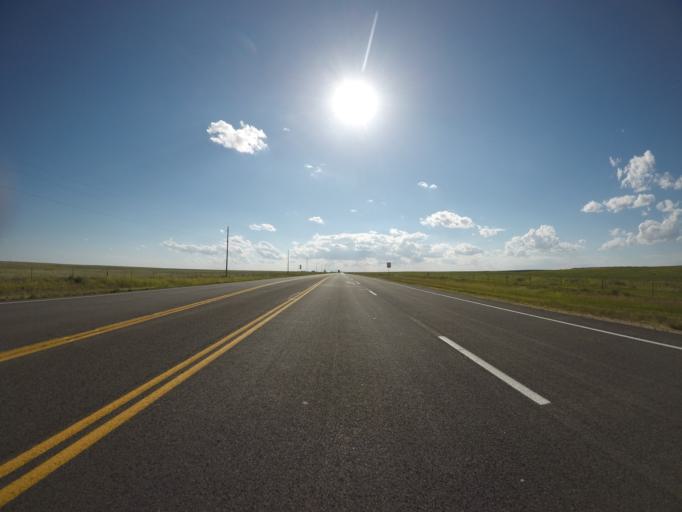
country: US
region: Colorado
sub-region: Morgan County
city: Fort Morgan
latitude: 40.6114
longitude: -103.8042
